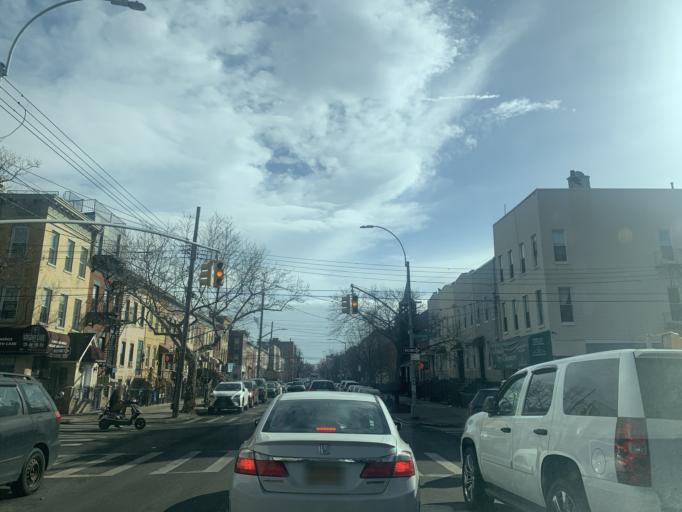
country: US
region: New York
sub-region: Kings County
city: East New York
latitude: 40.7047
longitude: -73.9168
